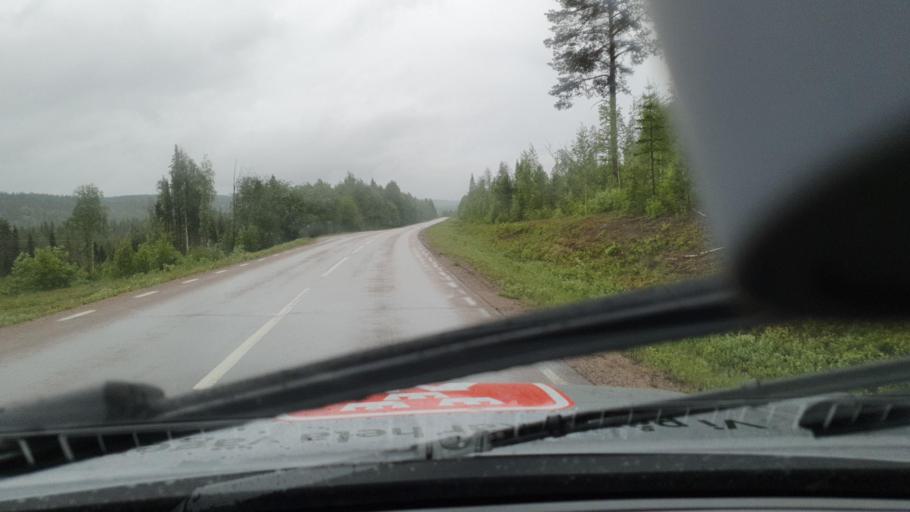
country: SE
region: Norrbotten
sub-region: Overtornea Kommun
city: OEvertornea
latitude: 66.4492
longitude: 23.3025
